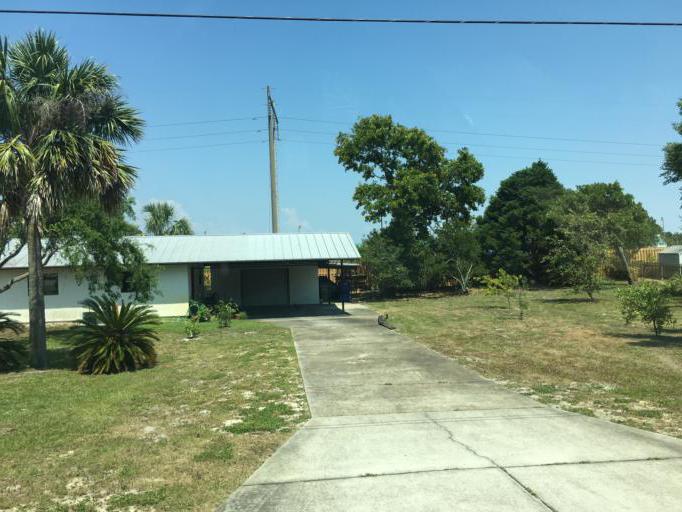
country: US
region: Florida
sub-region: Bay County
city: Laguna Beach
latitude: 30.2302
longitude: -85.8790
